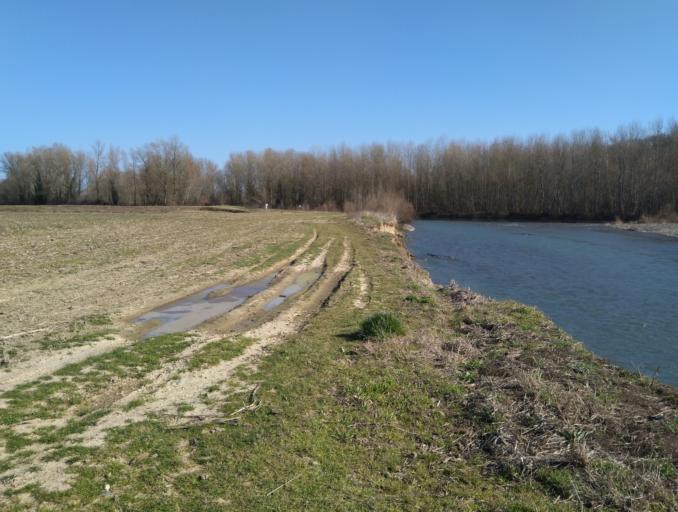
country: FR
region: Midi-Pyrenees
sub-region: Departement du Gers
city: Riscle
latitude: 43.6540
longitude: -0.1455
